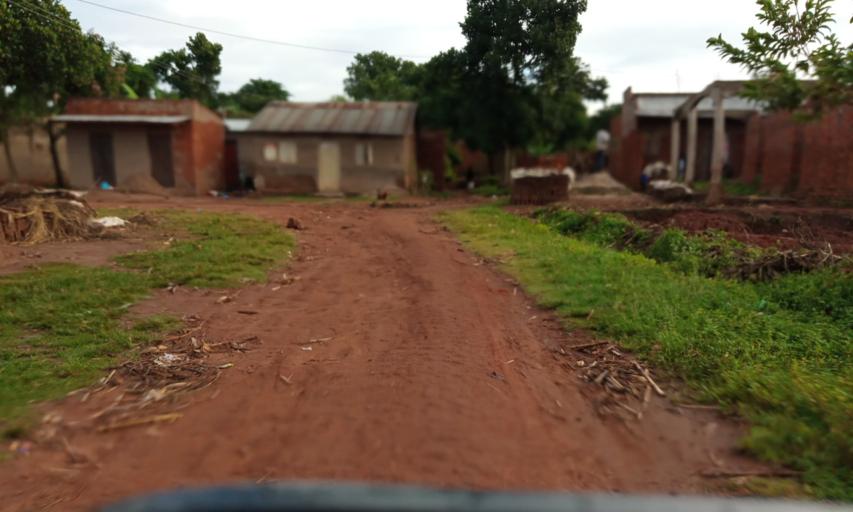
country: UG
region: Eastern Region
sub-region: Mbale District
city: Mbale
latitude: 1.1471
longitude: 34.1682
